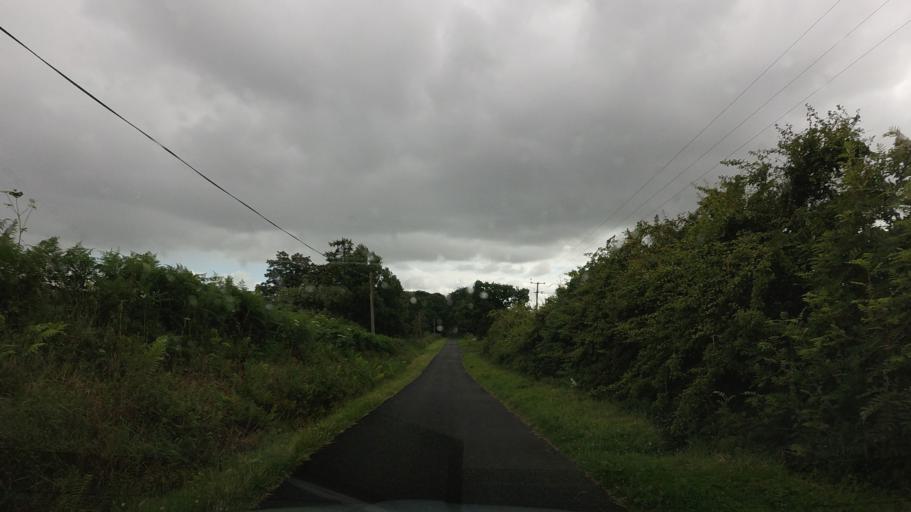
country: GB
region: Scotland
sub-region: Stirling
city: Killearn
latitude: 56.0730
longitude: -4.4505
